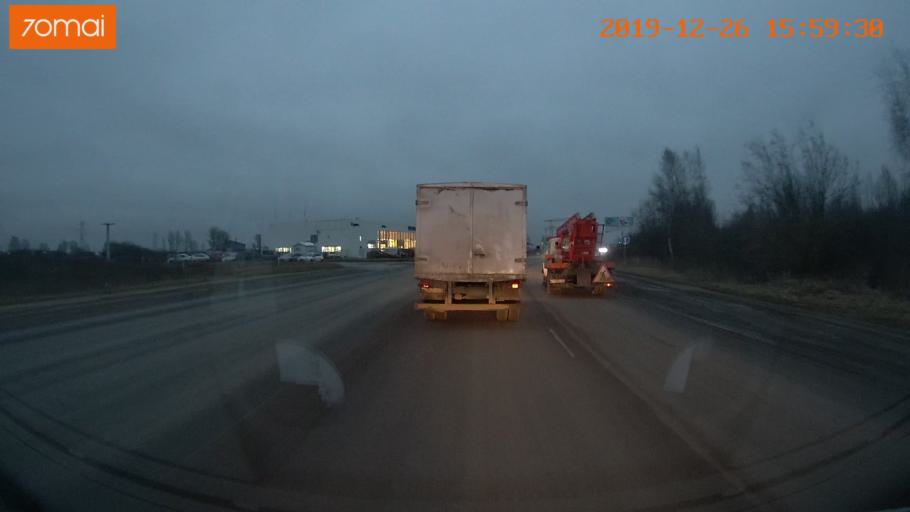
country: RU
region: Jaroslavl
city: Rybinsk
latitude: 58.0311
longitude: 38.8044
